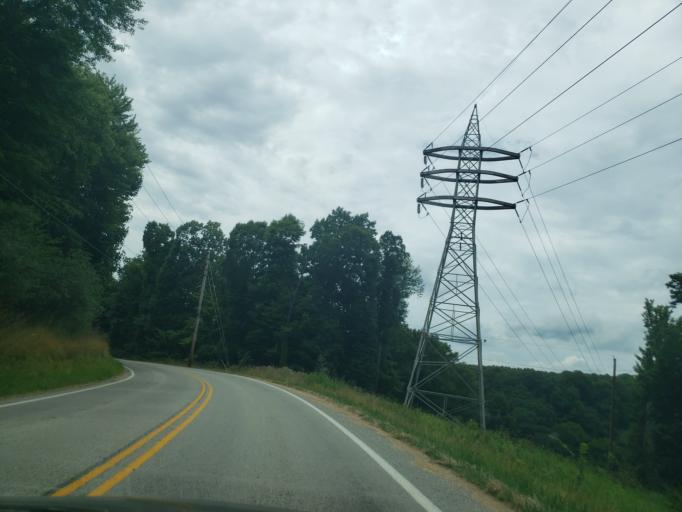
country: US
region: Pennsylvania
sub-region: Allegheny County
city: Emsworth
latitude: 40.5360
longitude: -80.0988
